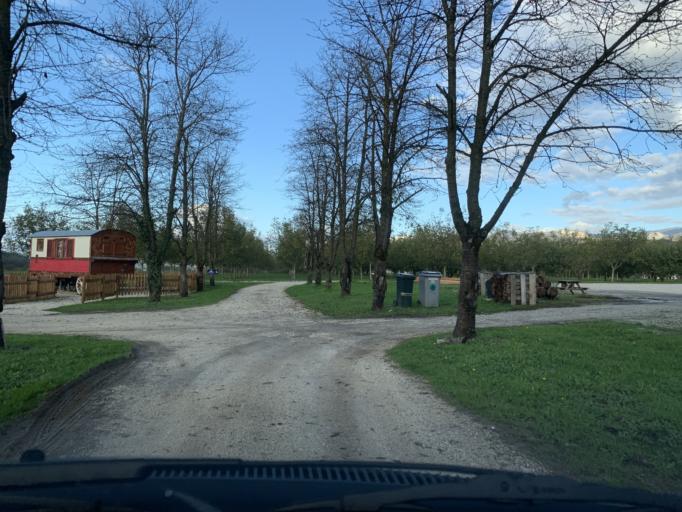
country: FR
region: Rhone-Alpes
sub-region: Departement de la Drome
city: Saint-Jean-en-Royans
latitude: 45.0305
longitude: 5.3004
